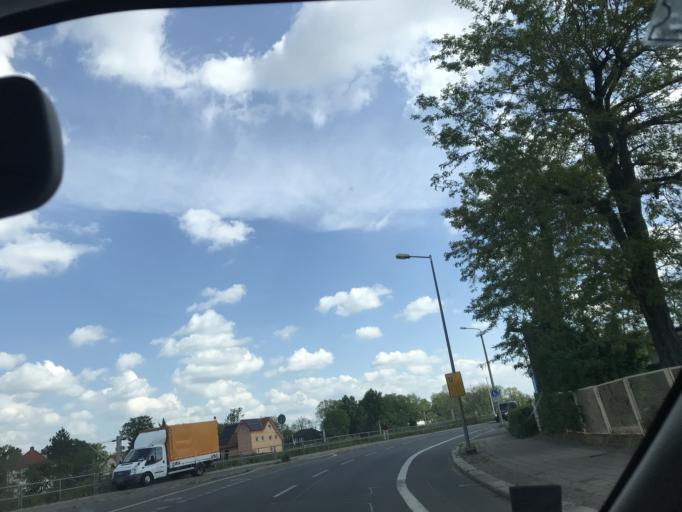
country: DE
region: Saxony
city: Leipzig
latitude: 51.3515
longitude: 12.3000
